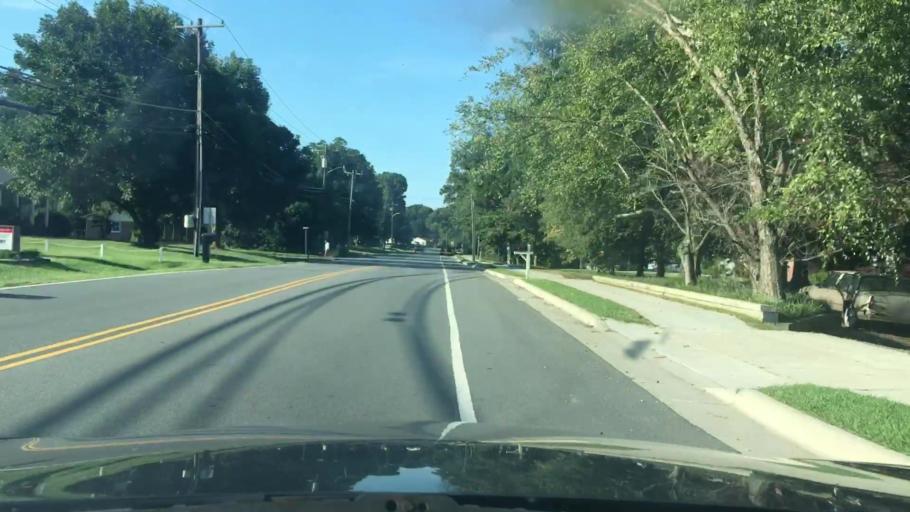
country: US
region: North Carolina
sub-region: Alamance County
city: Elon
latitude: 36.0963
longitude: -79.5079
